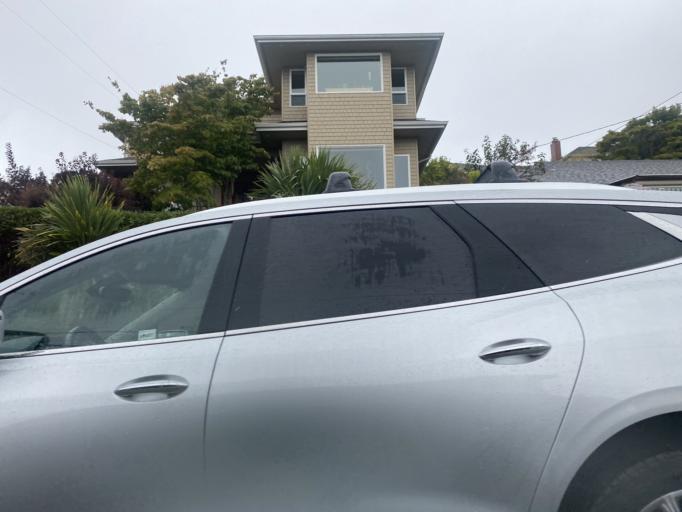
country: US
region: Washington
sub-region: King County
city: Seattle
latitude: 47.6469
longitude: -122.4047
